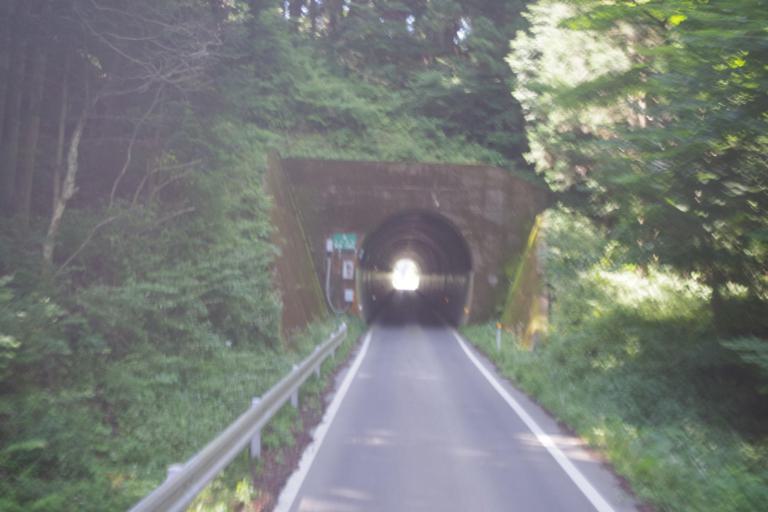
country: JP
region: Miyagi
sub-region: Oshika Gun
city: Onagawa Cho
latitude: 38.6693
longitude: 141.4433
